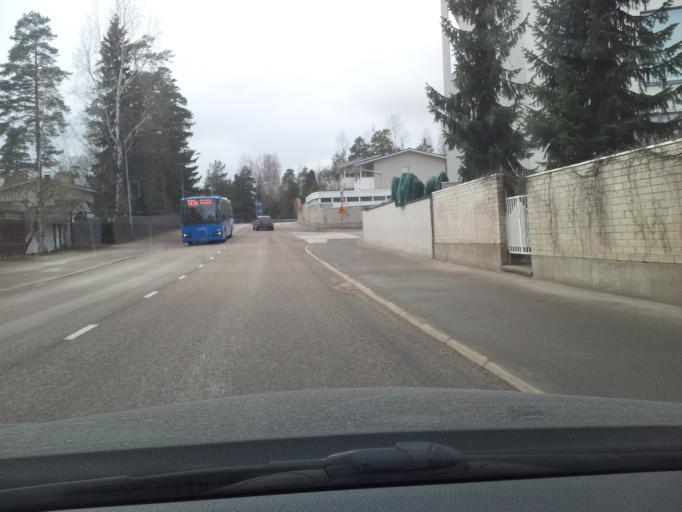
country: FI
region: Uusimaa
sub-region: Helsinki
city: Koukkuniemi
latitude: 60.1748
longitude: 24.7407
